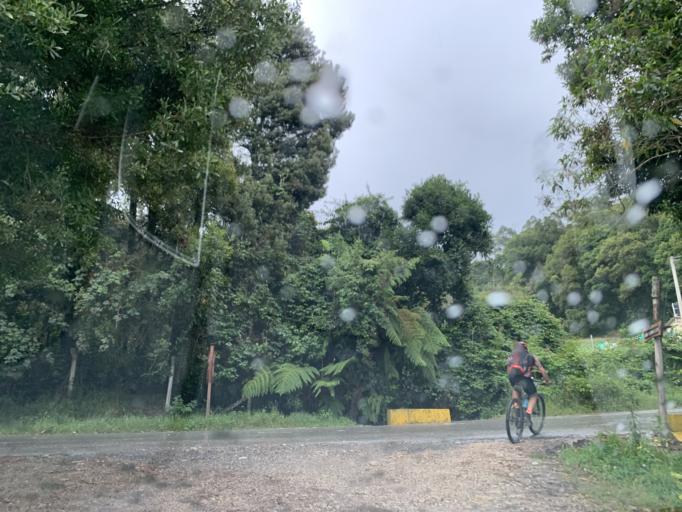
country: CO
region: Boyaca
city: Arcabuco
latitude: 5.7580
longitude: -73.4817
